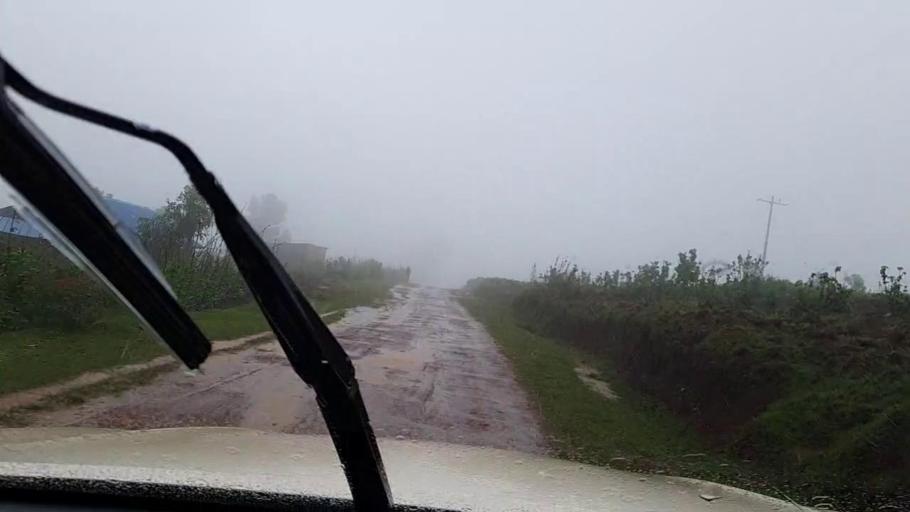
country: RW
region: Northern Province
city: Byumba
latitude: -1.7368
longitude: 30.0107
